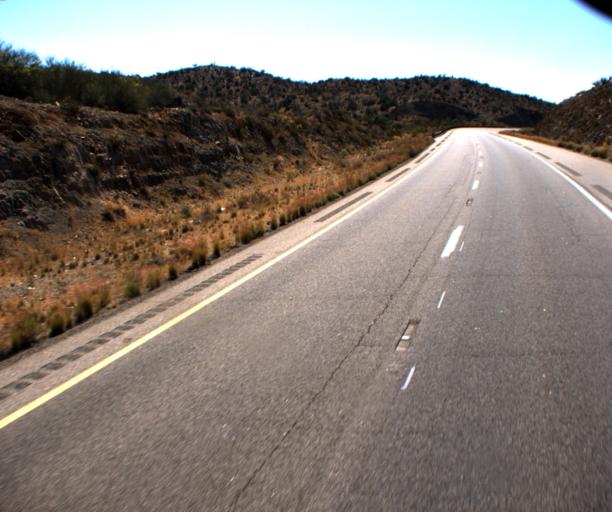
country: US
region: Arizona
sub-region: Yavapai County
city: Bagdad
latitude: 34.4573
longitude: -113.2929
